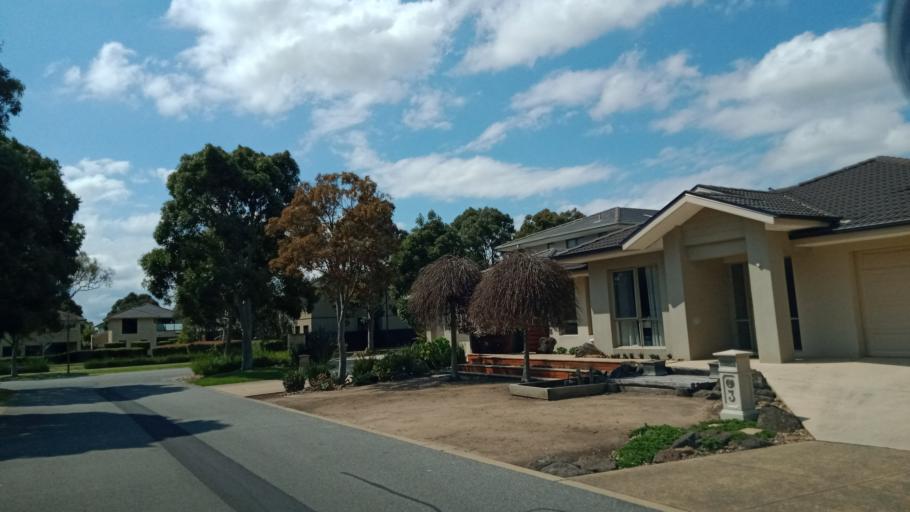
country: AU
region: Victoria
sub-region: Frankston
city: Sandhurst
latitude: -38.0841
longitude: 145.2020
